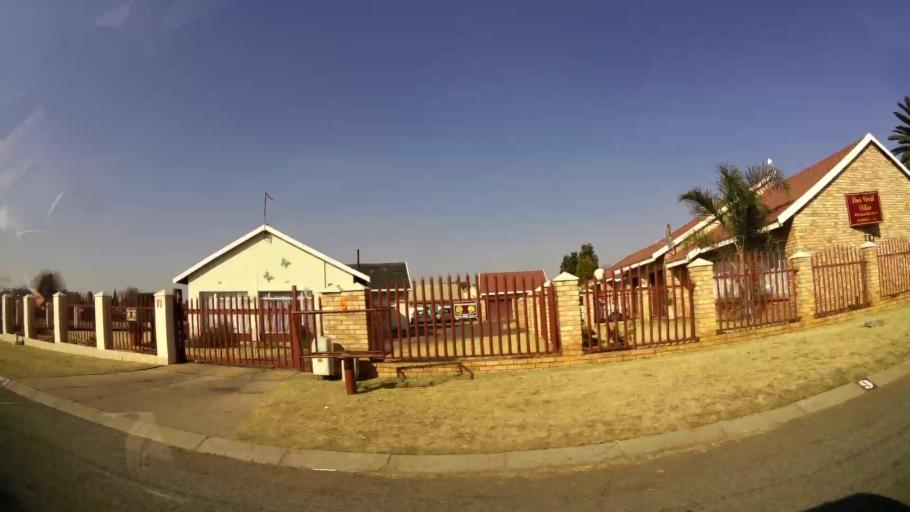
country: ZA
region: Gauteng
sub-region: West Rand District Municipality
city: Randfontein
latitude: -26.1779
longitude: 27.6887
